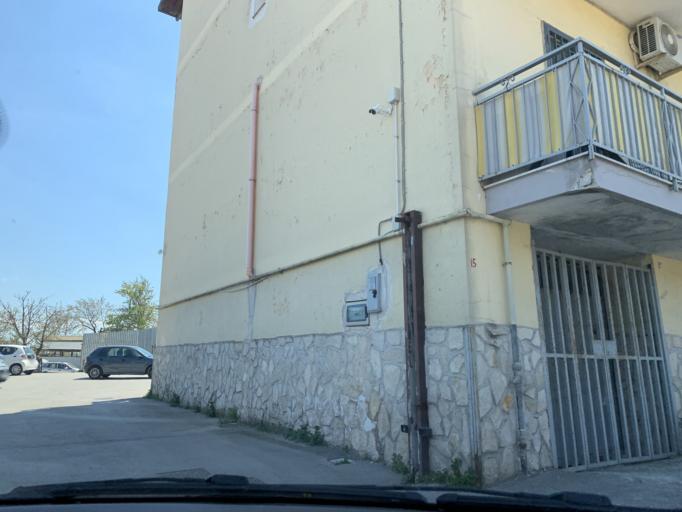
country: IT
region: Campania
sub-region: Provincia di Napoli
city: Napoli
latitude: 40.8777
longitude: 14.2362
